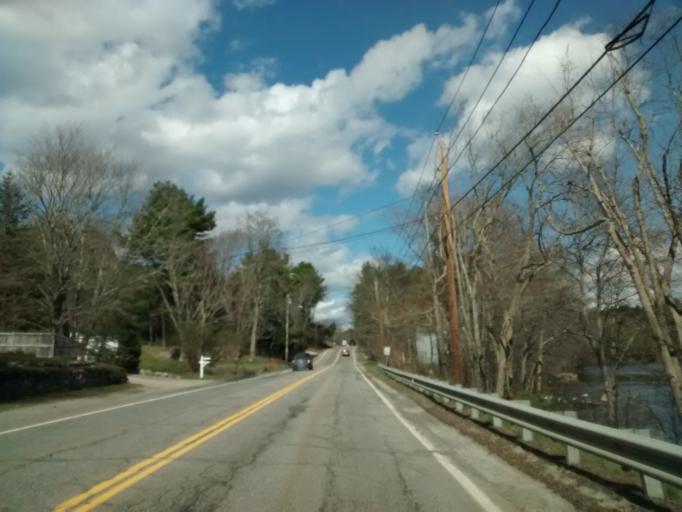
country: US
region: Massachusetts
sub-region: Worcester County
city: Upton
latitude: 42.1828
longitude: -71.6020
